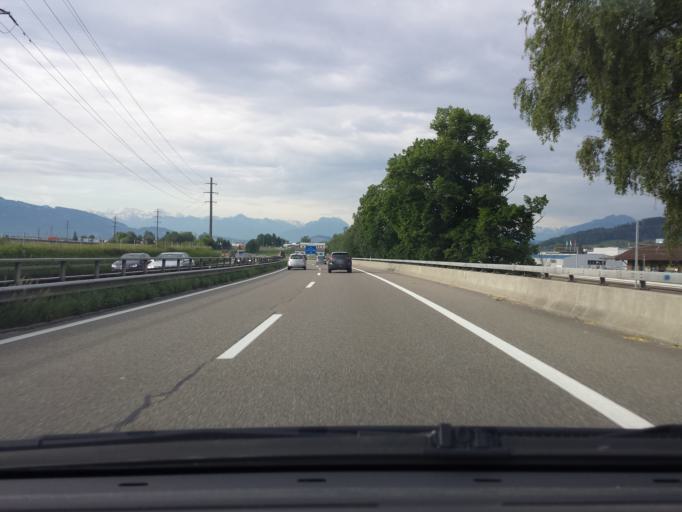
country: CH
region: Saint Gallen
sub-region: Wahlkreis Rheintal
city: Au
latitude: 47.4367
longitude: 9.6424
